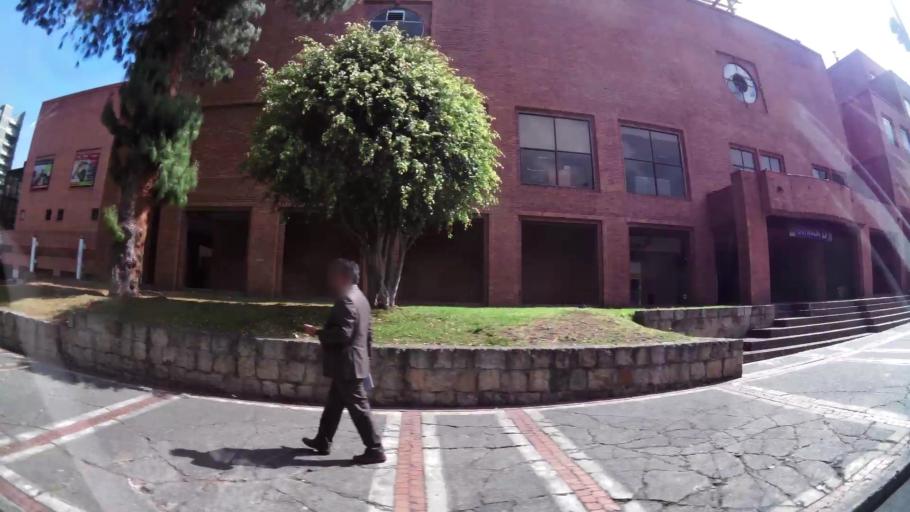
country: CO
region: Bogota D.C.
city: Barrio San Luis
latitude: 4.6920
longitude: -74.0325
